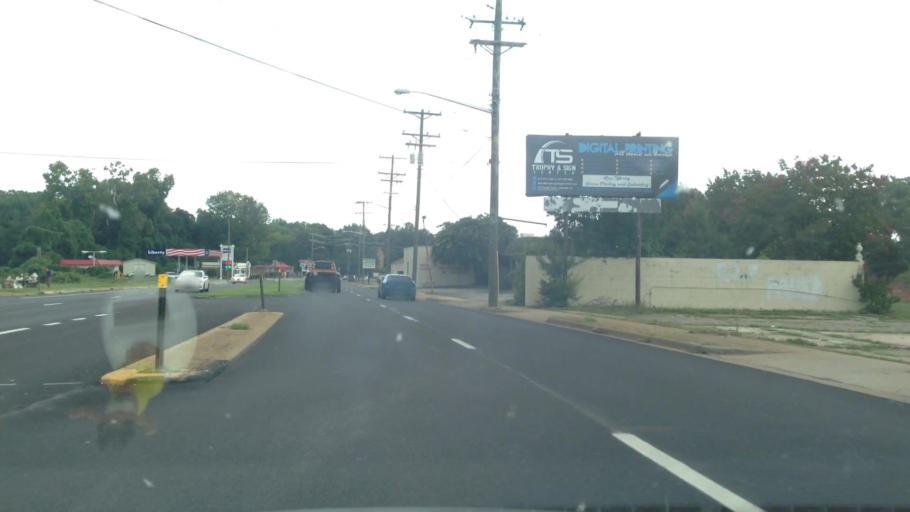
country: US
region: Virginia
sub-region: City of Danville
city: Danville
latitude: 36.5619
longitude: -79.4528
